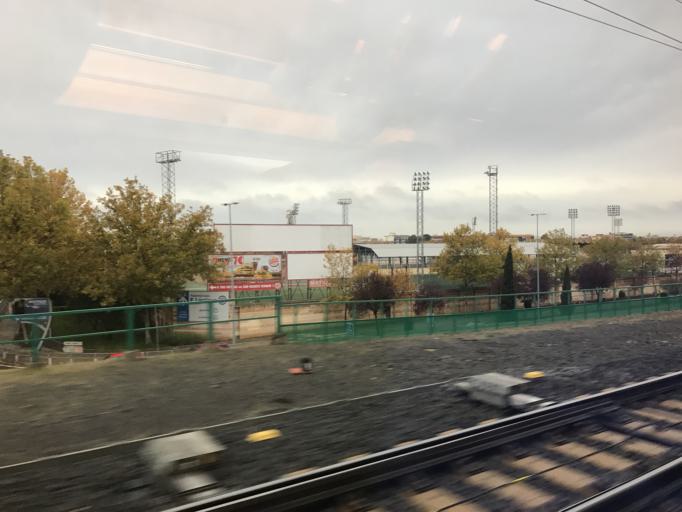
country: ES
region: Castille-La Mancha
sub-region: Provincia de Ciudad Real
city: Ciudad Real
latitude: 38.9876
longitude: -3.9146
